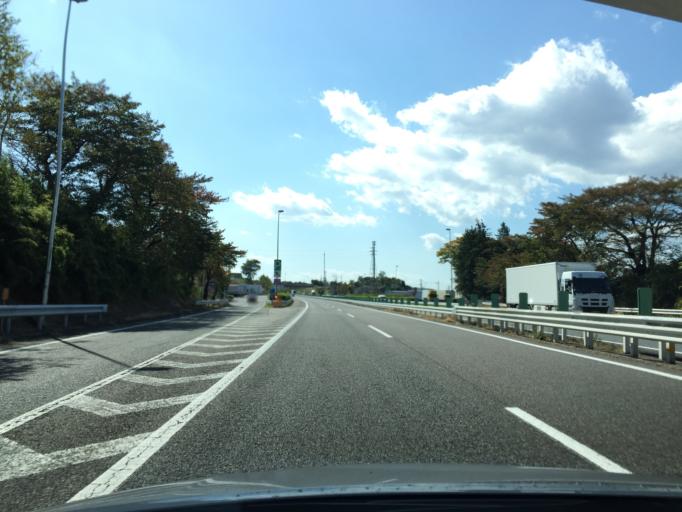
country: JP
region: Fukushima
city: Sukagawa
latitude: 37.2571
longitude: 140.3372
